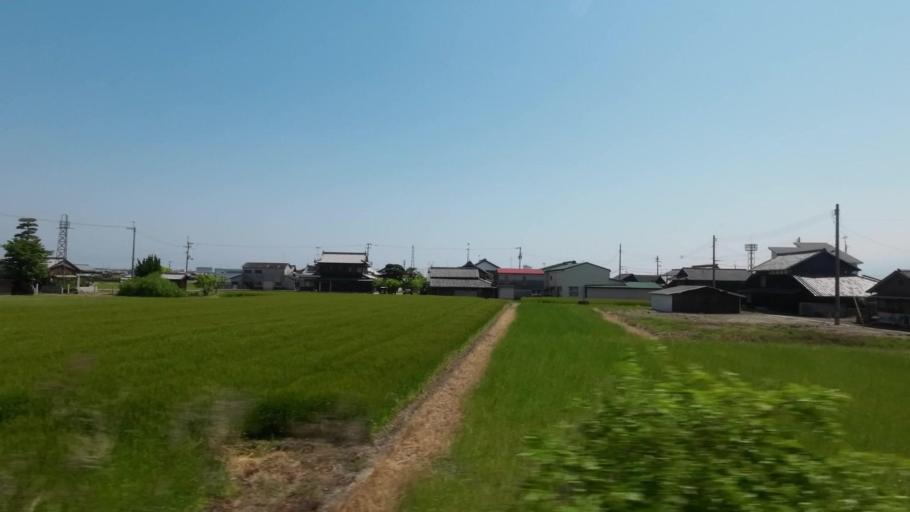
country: JP
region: Ehime
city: Saijo
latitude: 33.9195
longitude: 133.0946
